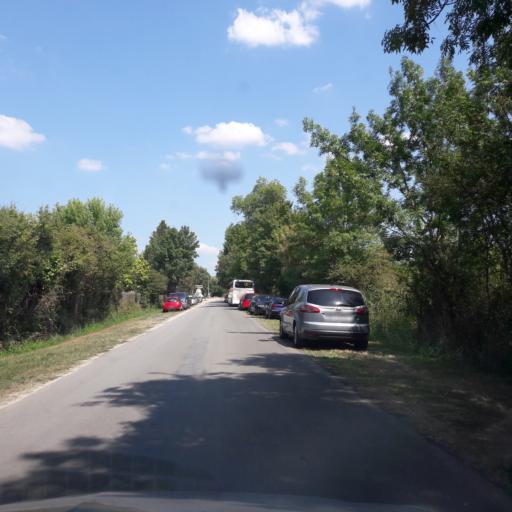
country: FR
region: Aquitaine
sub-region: Departement de la Gironde
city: Cadaujac
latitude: 44.7390
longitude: -0.5096
